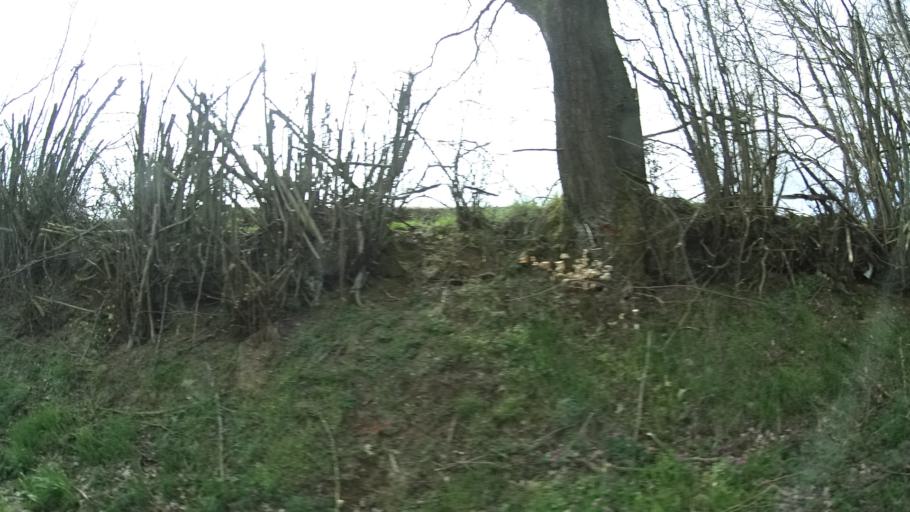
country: DE
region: Rheinland-Pfalz
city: Weitersbach
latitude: 49.8737
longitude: 7.3204
